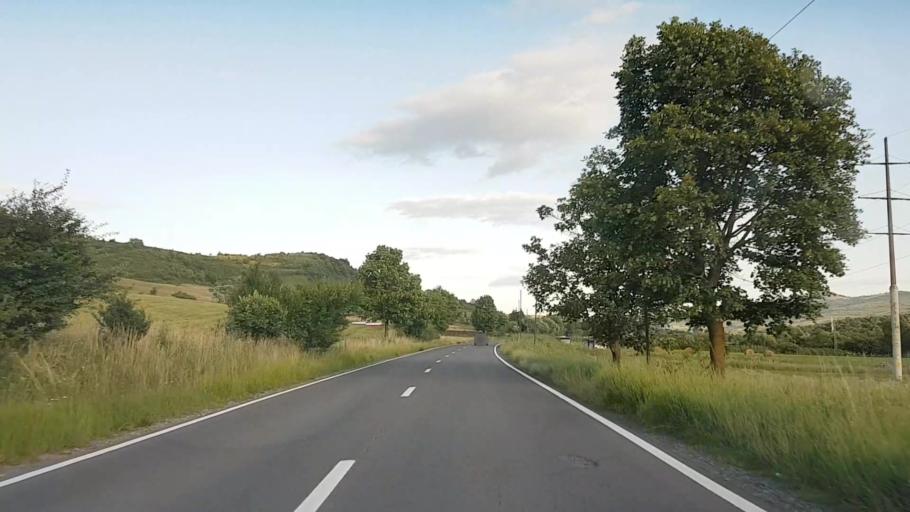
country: RO
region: Harghita
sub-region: Comuna Praid
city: Ocna de Sus
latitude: 46.5092
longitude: 25.1598
